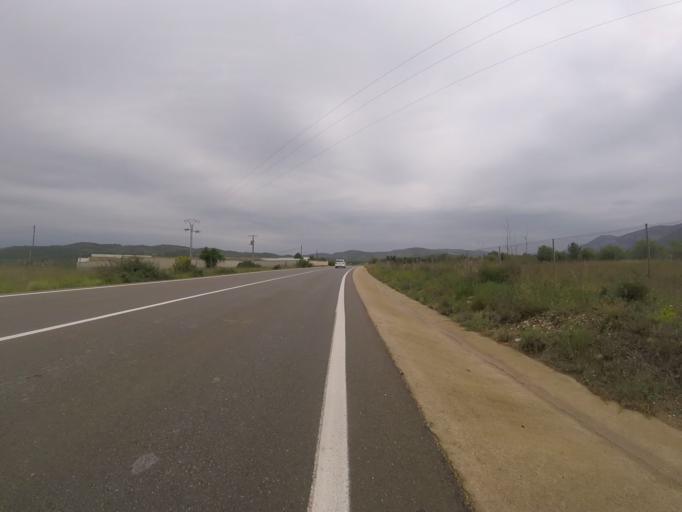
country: ES
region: Valencia
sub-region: Provincia de Castello
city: Alcoceber
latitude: 40.2528
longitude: 0.2461
